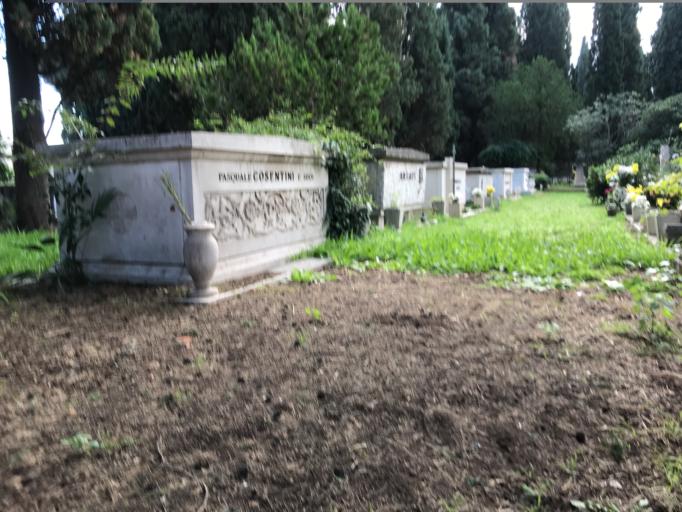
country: IT
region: Latium
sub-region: Citta metropolitana di Roma Capitale
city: Rome
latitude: 41.9076
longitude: 12.5308
